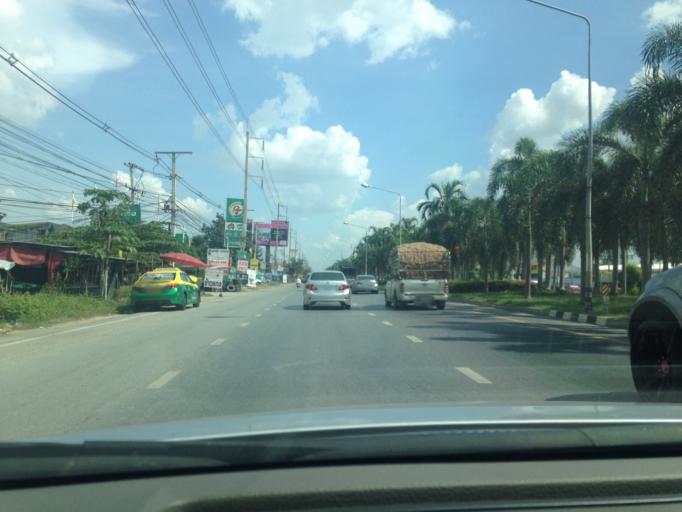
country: TH
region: Phra Nakhon Si Ayutthaya
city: Ban Bang Kadi Pathum Thani
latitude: 13.9997
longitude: 100.5714
